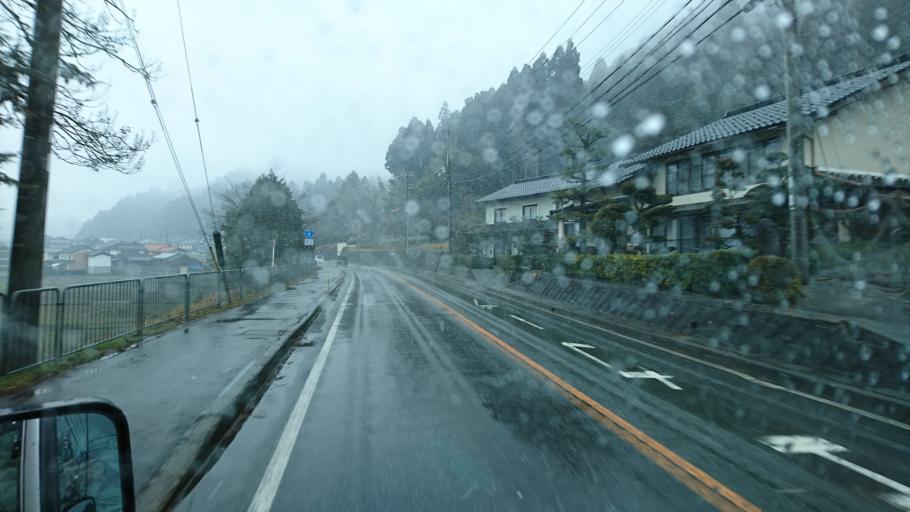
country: JP
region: Hyogo
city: Toyooka
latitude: 35.3804
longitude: 134.6523
